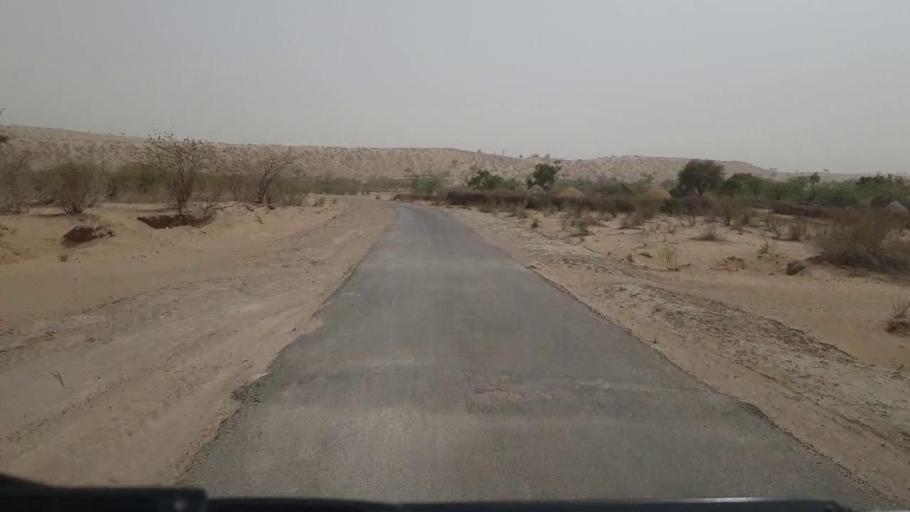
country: PK
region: Sindh
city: Islamkot
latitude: 25.2661
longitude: 70.6493
